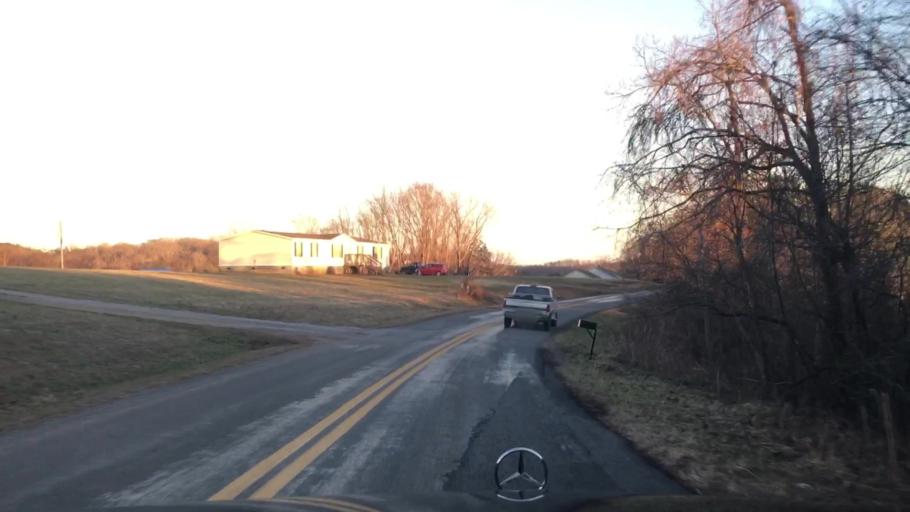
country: US
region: Virginia
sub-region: Pittsylvania County
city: Hurt
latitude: 37.1124
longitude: -79.3137
